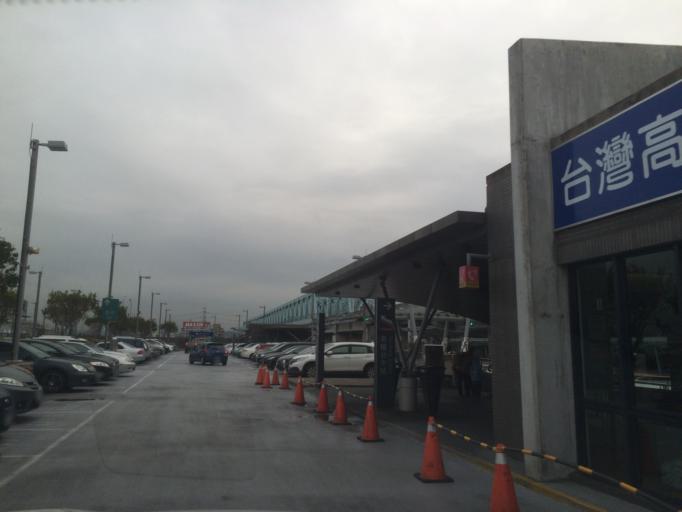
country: TW
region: Taiwan
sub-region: Changhua
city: Chang-hua
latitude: 24.1114
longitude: 120.6166
